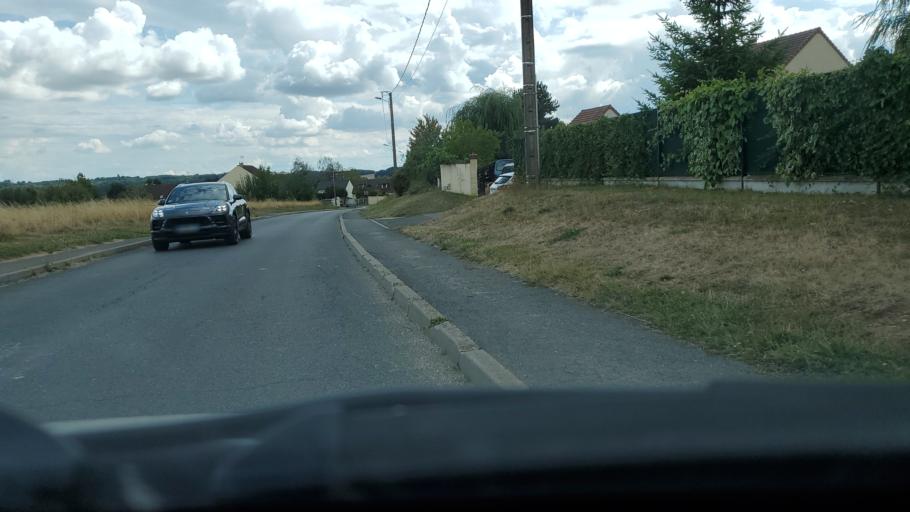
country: FR
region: Ile-de-France
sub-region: Departement de Seine-et-Marne
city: Mouroux
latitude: 48.8295
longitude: 3.0354
